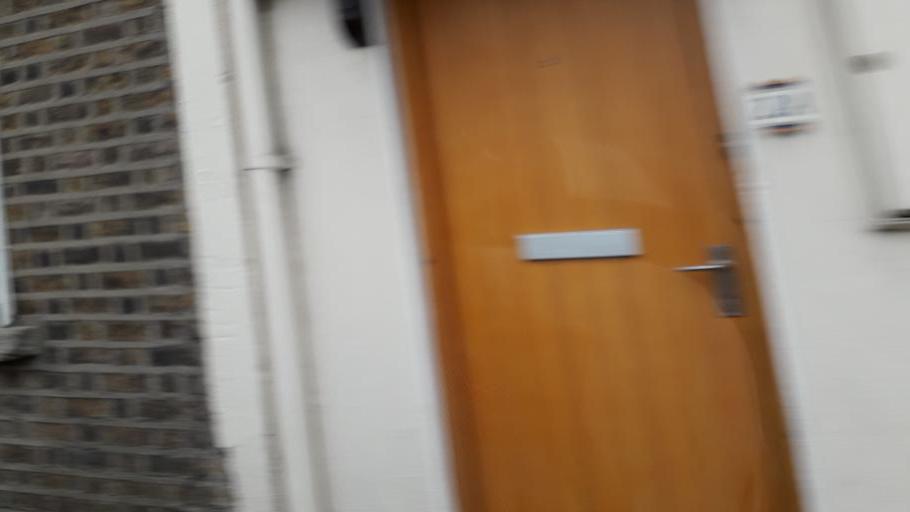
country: IE
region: Leinster
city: Rathgar
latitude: 53.3294
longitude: -6.2784
